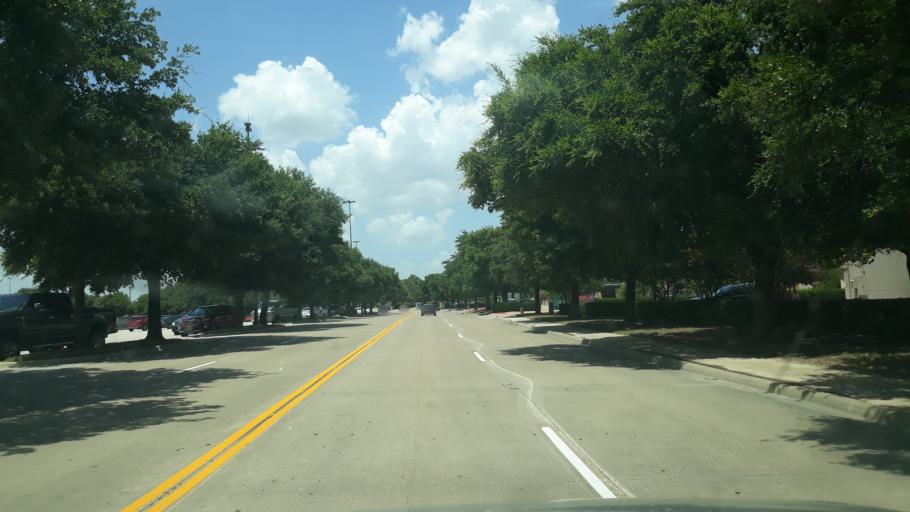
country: US
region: Texas
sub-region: Dallas County
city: Coppell
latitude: 32.9667
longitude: -97.0391
